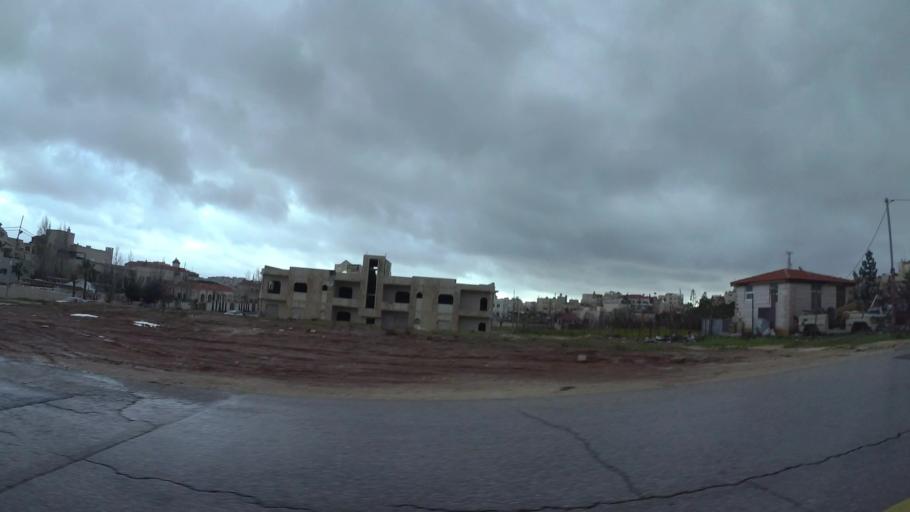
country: JO
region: Amman
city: Al Jubayhah
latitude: 32.0377
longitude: 35.8636
